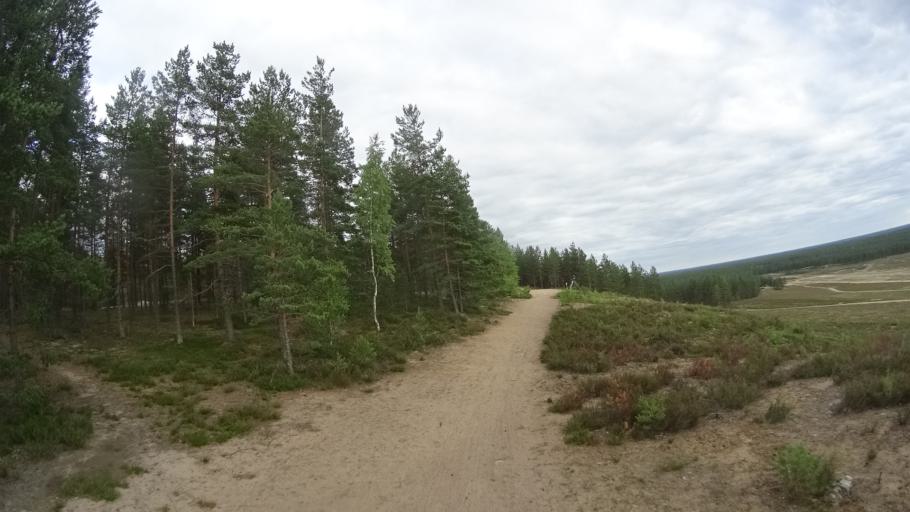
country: FI
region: Satakunta
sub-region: Pohjois-Satakunta
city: Jaemijaervi
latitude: 61.7762
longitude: 22.7202
